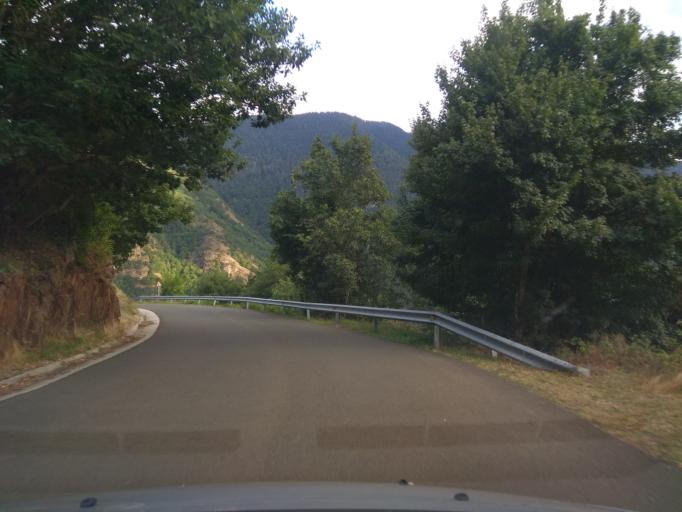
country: ES
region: Catalonia
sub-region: Provincia de Lleida
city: Les
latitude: 42.8329
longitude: 0.7208
